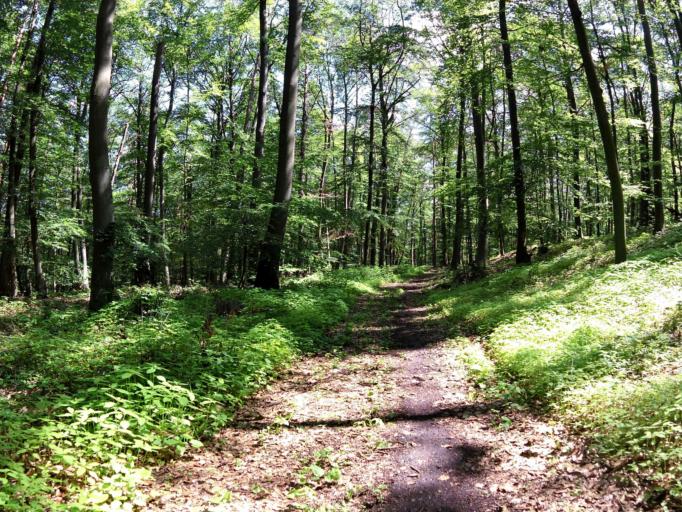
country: DE
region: Bavaria
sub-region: Regierungsbezirk Unterfranken
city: Eibelstadt
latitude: 49.7322
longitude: 10.0070
